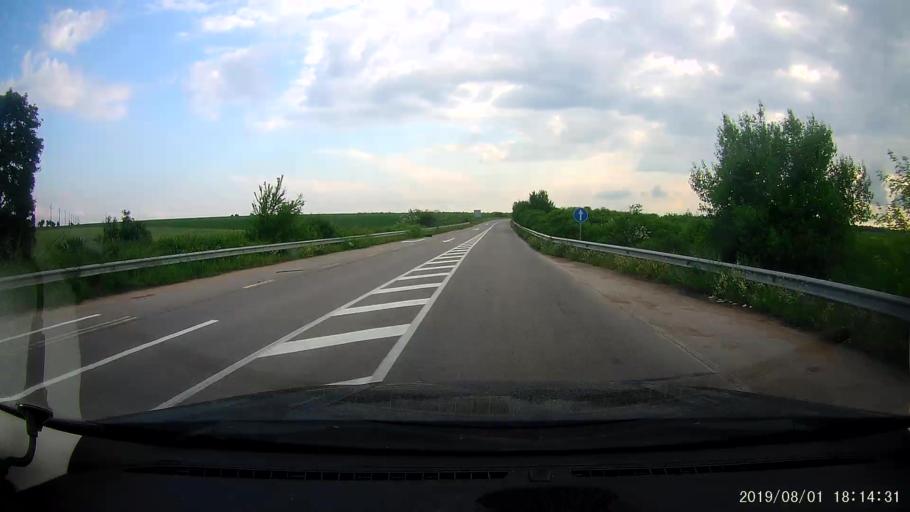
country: BG
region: Silistra
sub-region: Obshtina Dulovo
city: Dulovo
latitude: 43.7676
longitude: 27.1248
